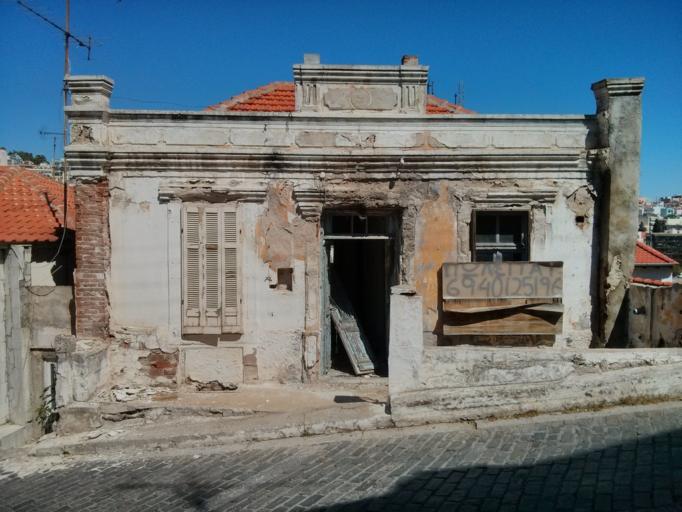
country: GR
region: East Macedonia and Thrace
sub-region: Nomos Kavalas
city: Kavala
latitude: 40.9356
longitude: 24.4165
